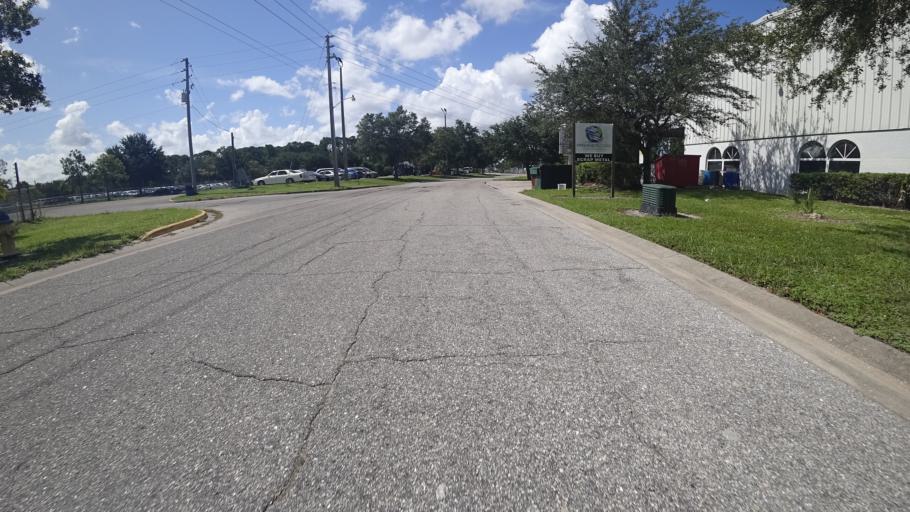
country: US
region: Florida
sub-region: Manatee County
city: Samoset
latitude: 27.4338
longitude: -82.5340
